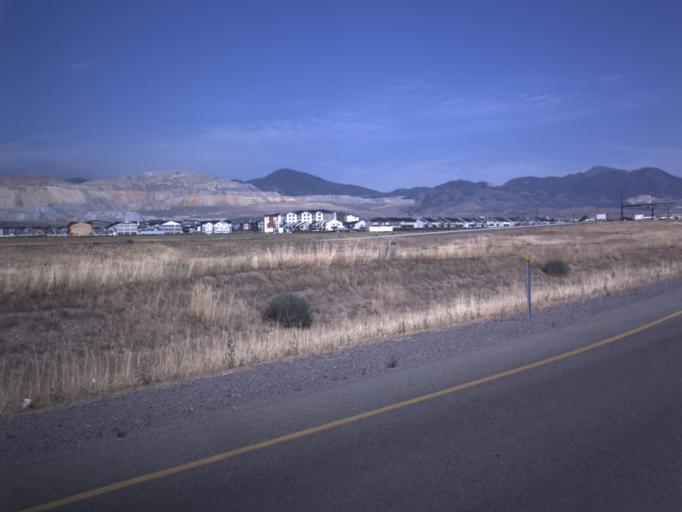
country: US
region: Utah
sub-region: Salt Lake County
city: Herriman
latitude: 40.5332
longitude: -112.0109
